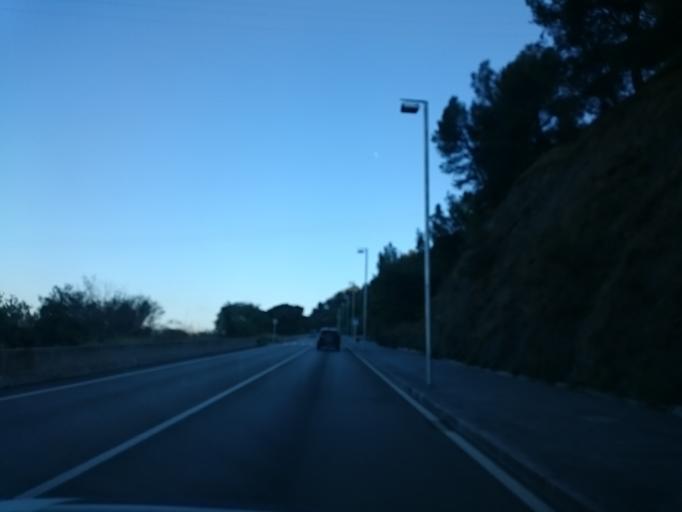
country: ES
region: Catalonia
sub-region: Provincia de Barcelona
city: Martorell
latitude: 41.4702
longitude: 1.9405
